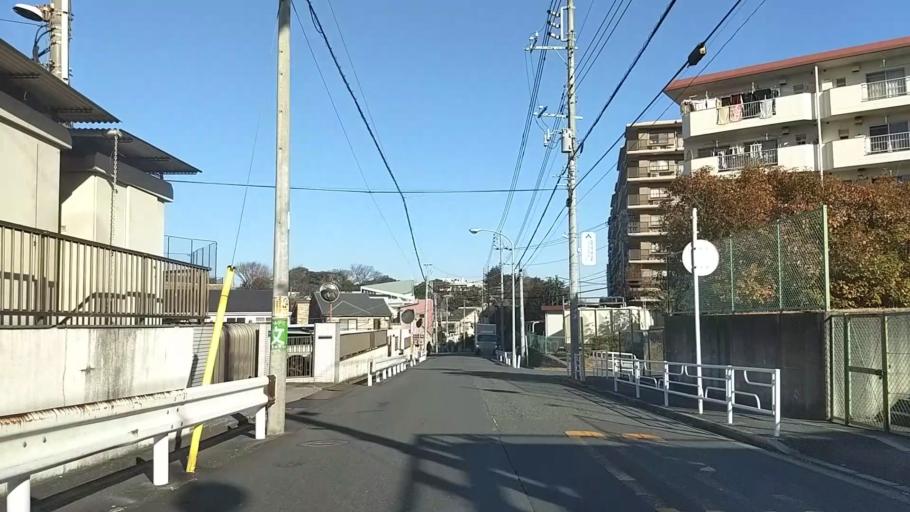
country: JP
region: Kanagawa
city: Yokohama
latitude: 35.4228
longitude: 139.6119
